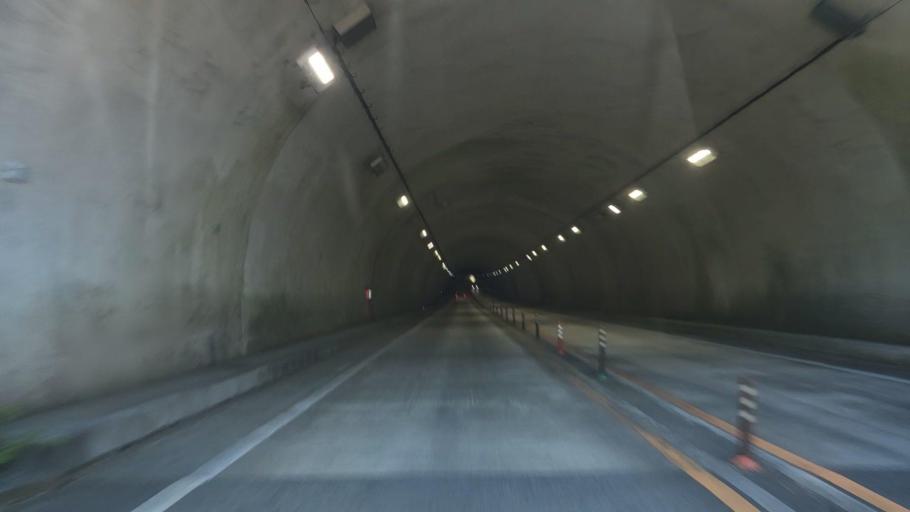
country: JP
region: Wakayama
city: Shingu
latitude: 33.6082
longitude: 135.9166
